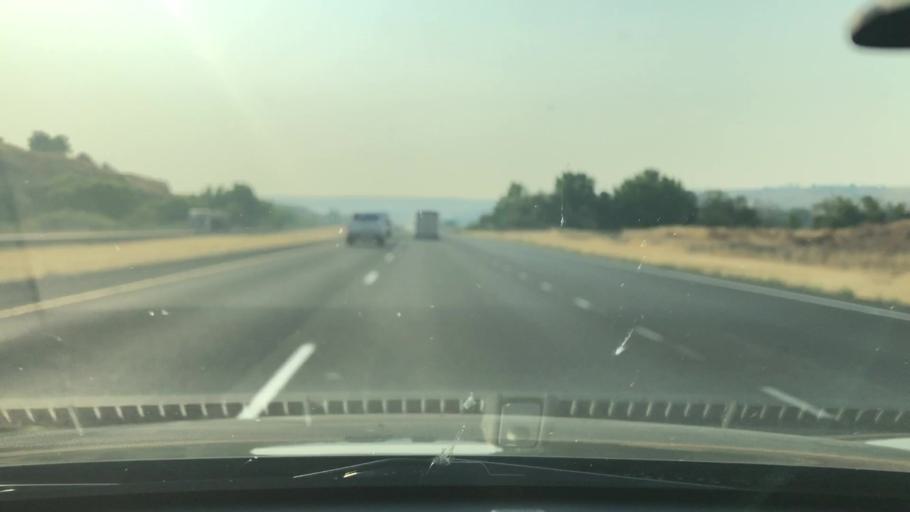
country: US
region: Oregon
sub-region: Umatilla County
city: Pendleton
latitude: 45.6655
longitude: -118.8134
